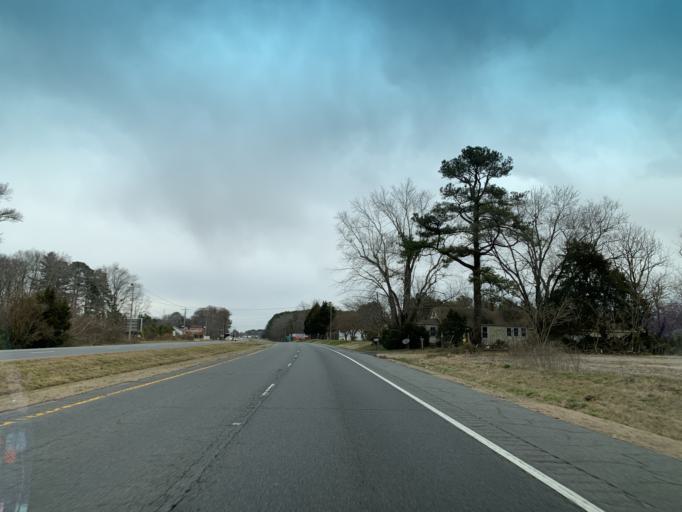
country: US
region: Virginia
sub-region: Accomack County
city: Wattsville
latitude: 37.9584
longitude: -75.5336
